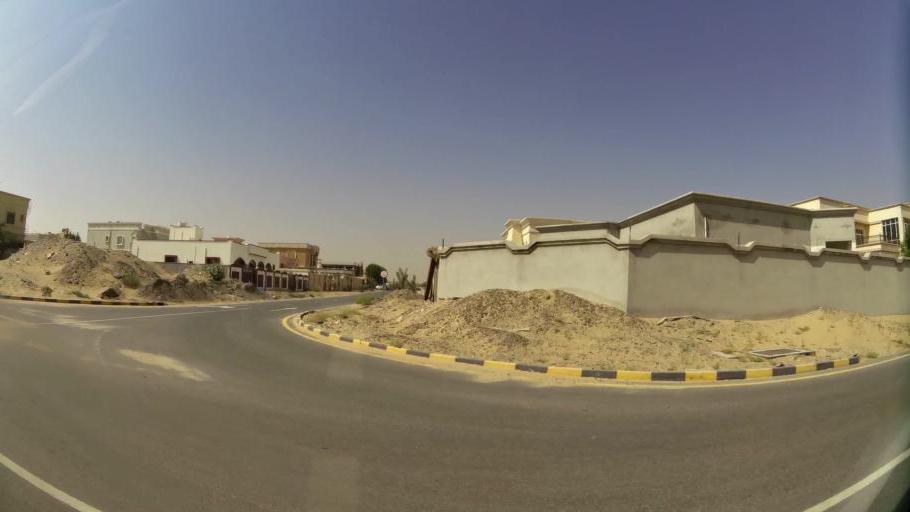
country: AE
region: Ajman
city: Ajman
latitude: 25.4095
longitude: 55.5352
